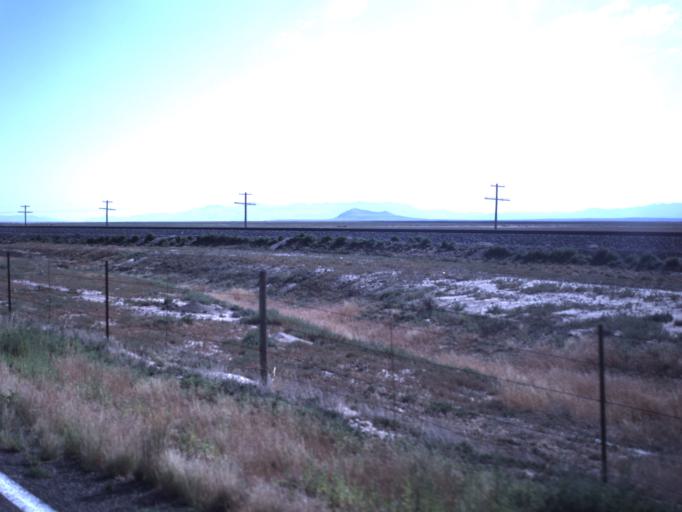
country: US
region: Utah
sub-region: Millard County
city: Delta
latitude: 39.0078
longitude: -112.7844
